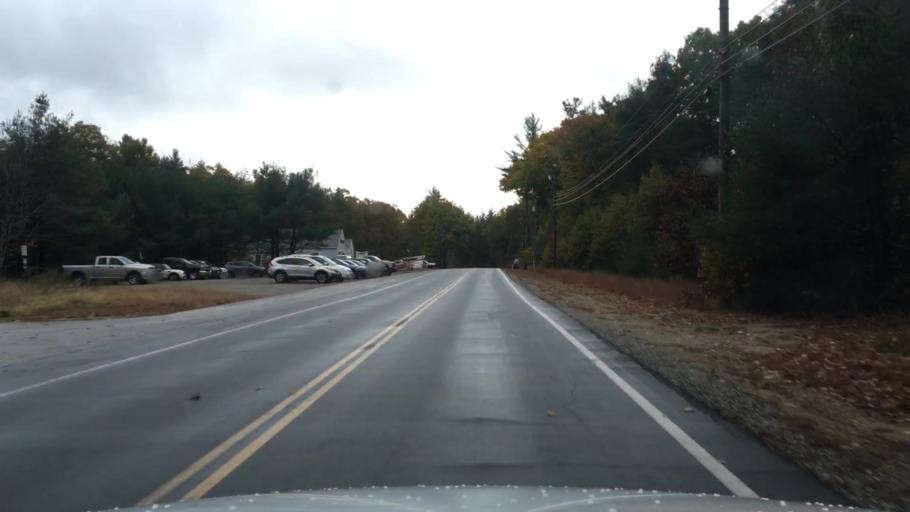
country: US
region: New Hampshire
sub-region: Strafford County
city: Lee
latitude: 43.1272
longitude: -71.0213
